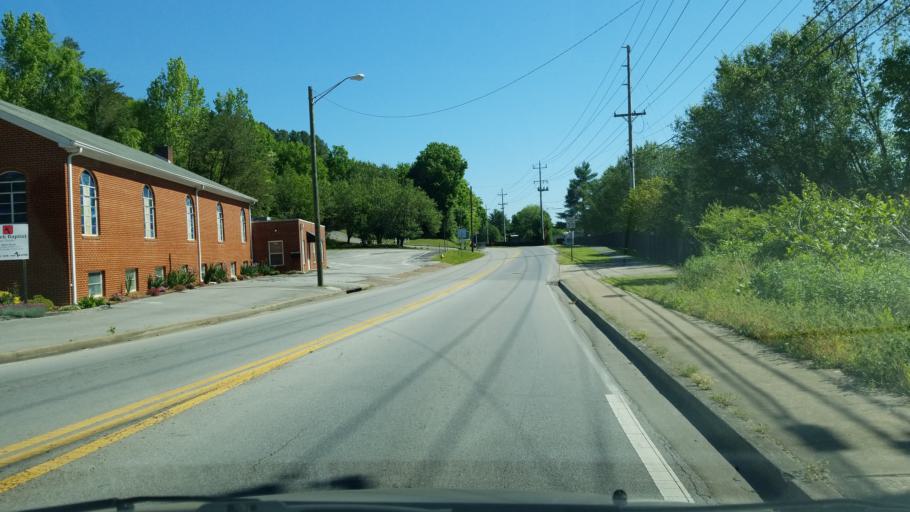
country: US
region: Tennessee
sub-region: Hamilton County
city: Signal Mountain
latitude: 35.1075
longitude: -85.3260
